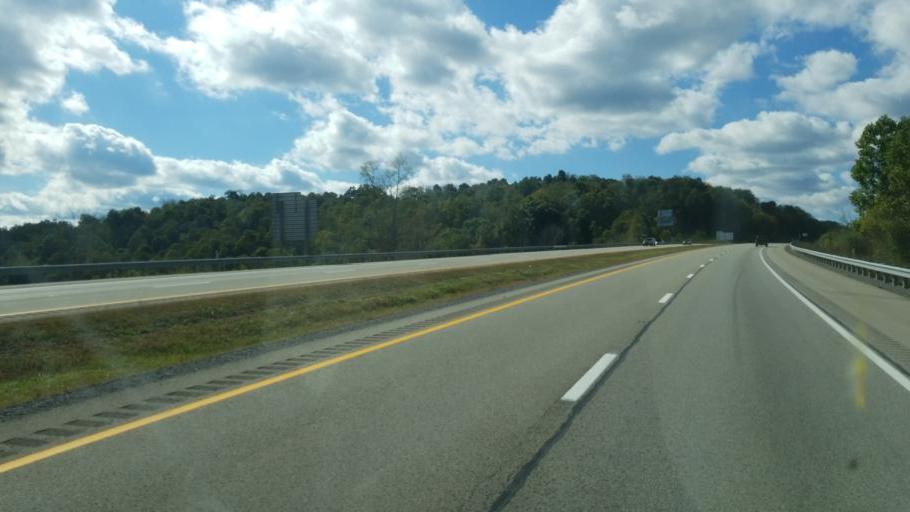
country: US
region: West Virginia
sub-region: Preston County
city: Kingwood
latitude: 39.6570
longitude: -79.6540
